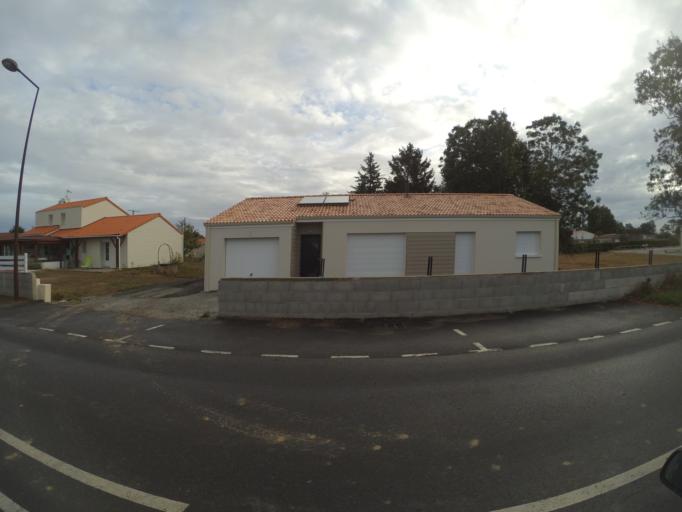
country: FR
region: Pays de la Loire
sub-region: Departement de la Loire-Atlantique
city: La Planche
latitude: 47.0137
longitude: -1.4309
